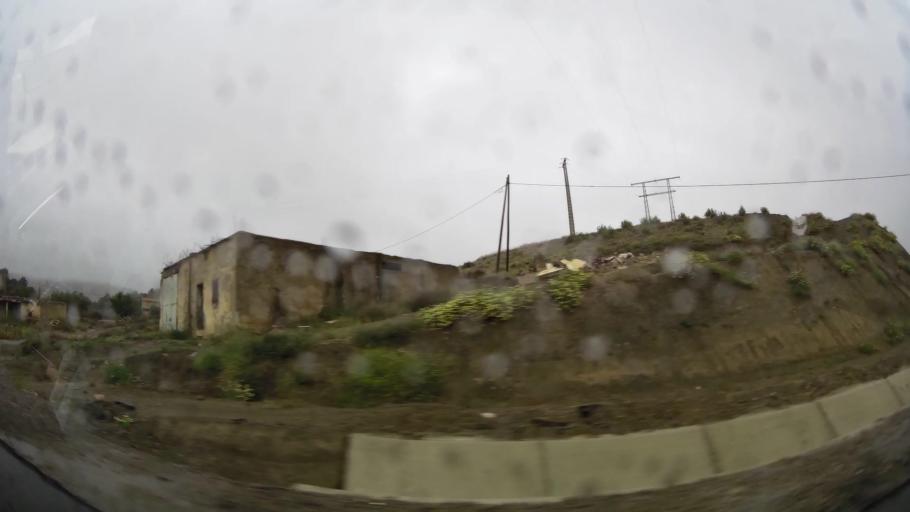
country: MA
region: Taza-Al Hoceima-Taounate
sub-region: Taza
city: Aknoul
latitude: 34.7941
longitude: -3.7467
